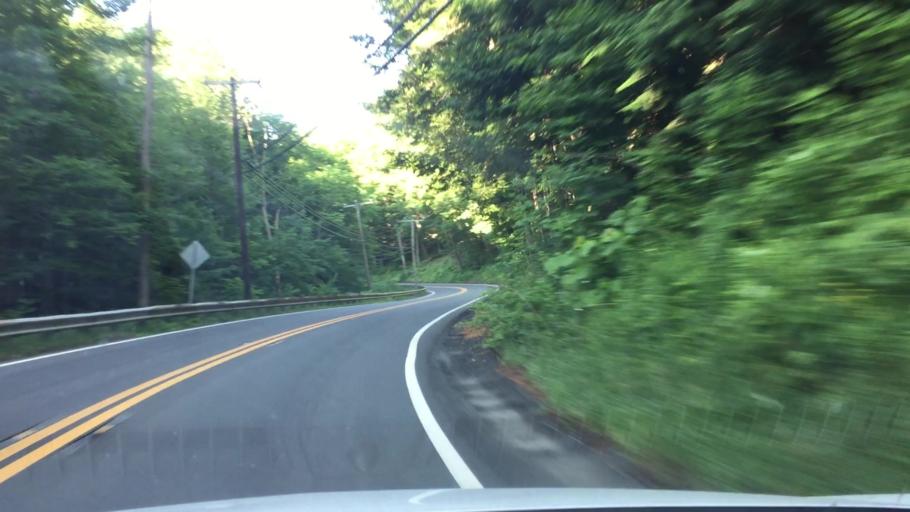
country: US
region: Massachusetts
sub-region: Berkshire County
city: Becket
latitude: 42.3183
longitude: -73.0925
